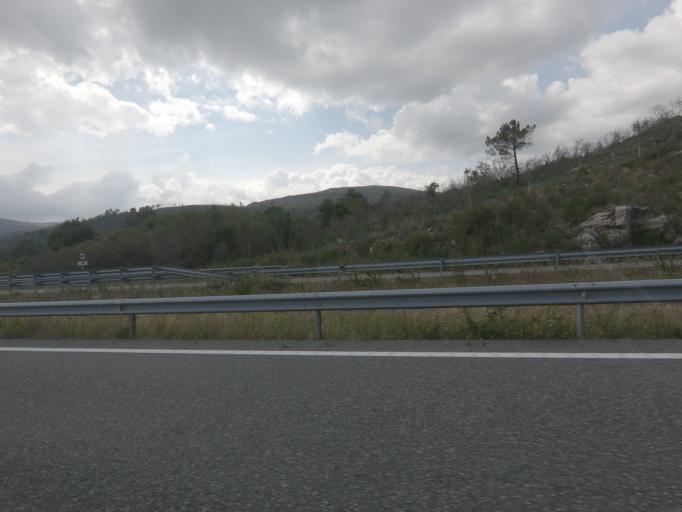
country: ES
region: Galicia
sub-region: Provincia de Ourense
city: Melon
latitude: 42.2713
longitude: -8.2043
